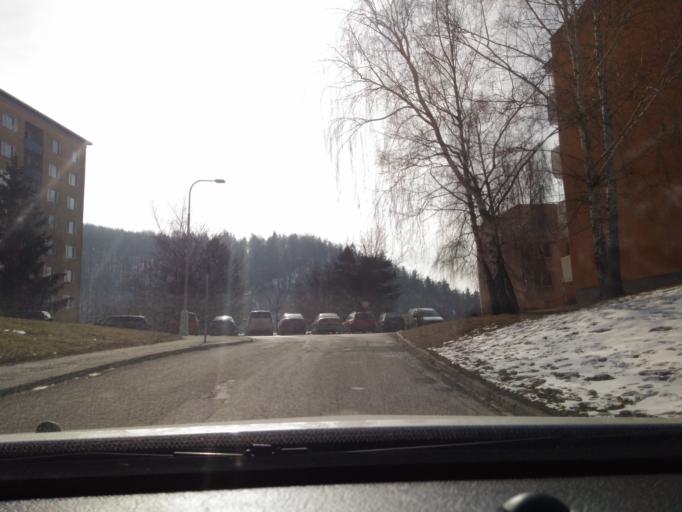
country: CZ
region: South Moravian
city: Troubsko
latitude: 49.2208
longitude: 16.5281
